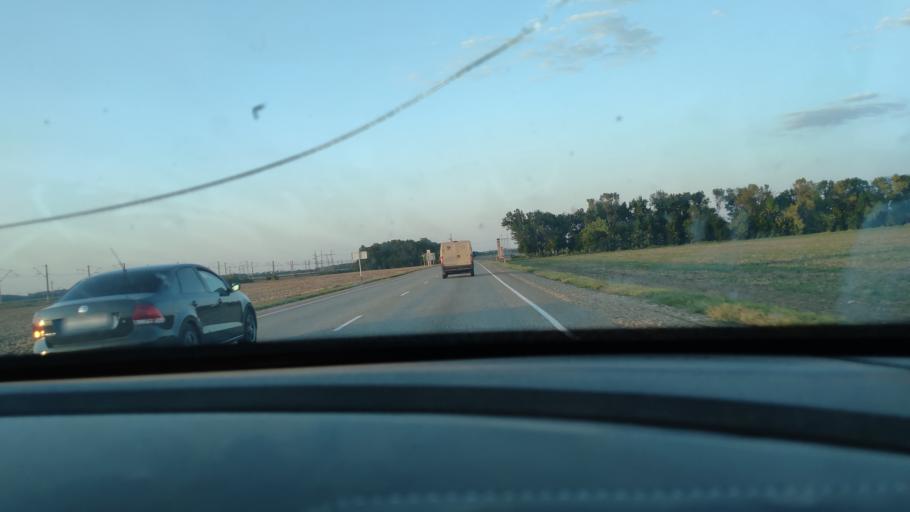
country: RU
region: Krasnodarskiy
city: Novominskaya
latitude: 46.3925
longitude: 38.9910
